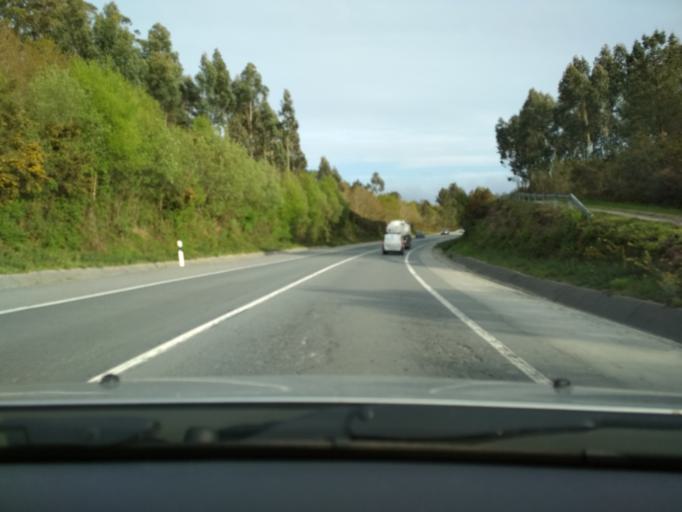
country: ES
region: Galicia
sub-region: Provincia da Coruna
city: Cerceda
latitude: 43.2238
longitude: -8.4594
